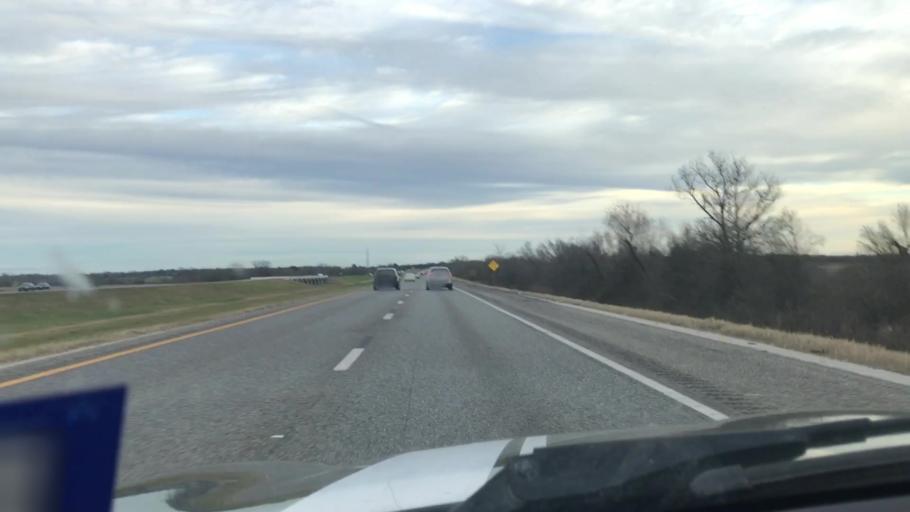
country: US
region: Texas
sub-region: Waller County
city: Hempstead
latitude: 30.1298
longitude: -96.1606
